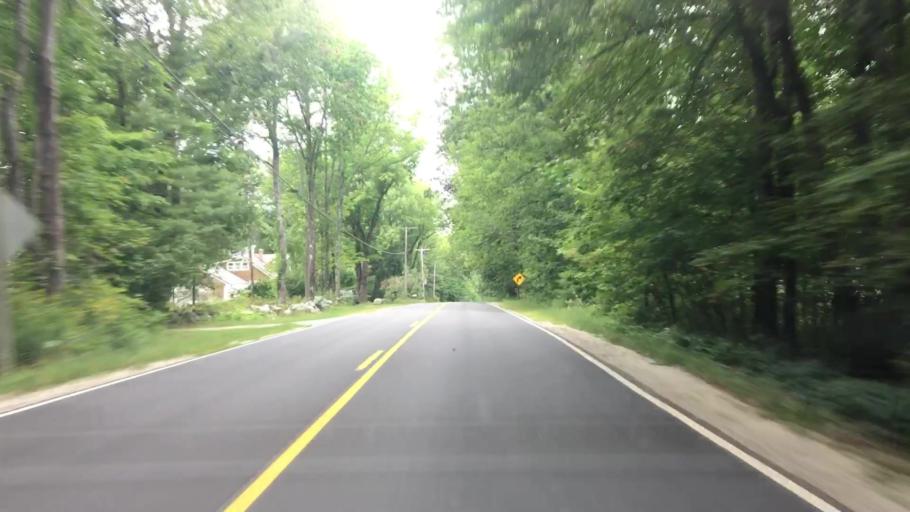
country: US
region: Maine
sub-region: Cumberland County
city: New Gloucester
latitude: 43.9136
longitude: -70.2510
